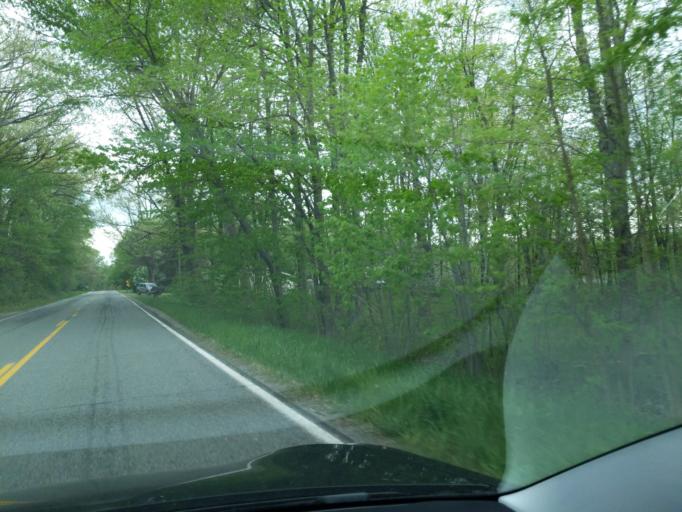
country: US
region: Michigan
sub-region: Ingham County
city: Stockbridge
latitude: 42.5087
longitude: -84.2680
